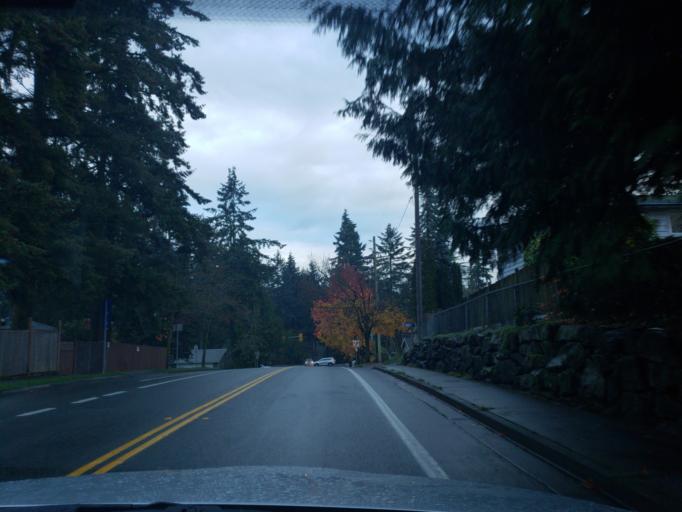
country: US
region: Washington
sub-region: King County
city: Shoreline
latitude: 47.7741
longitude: -122.3366
